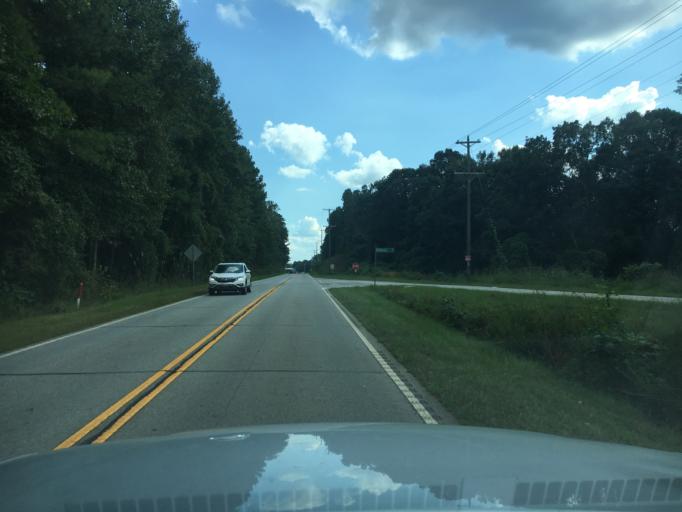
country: US
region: South Carolina
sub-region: Pickens County
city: Clemson
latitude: 34.7015
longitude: -82.8809
